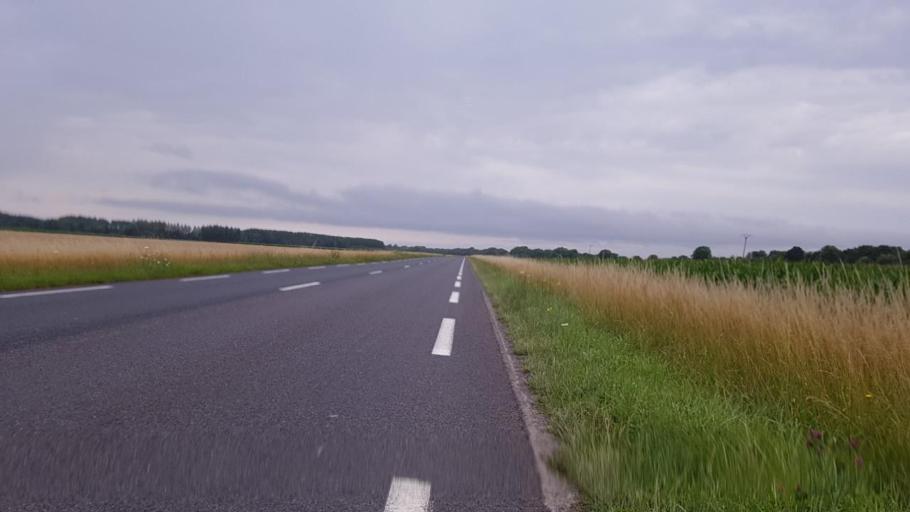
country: FR
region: Champagne-Ardenne
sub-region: Departement de la Marne
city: Pargny-sur-Saulx
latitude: 48.7566
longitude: 4.7333
